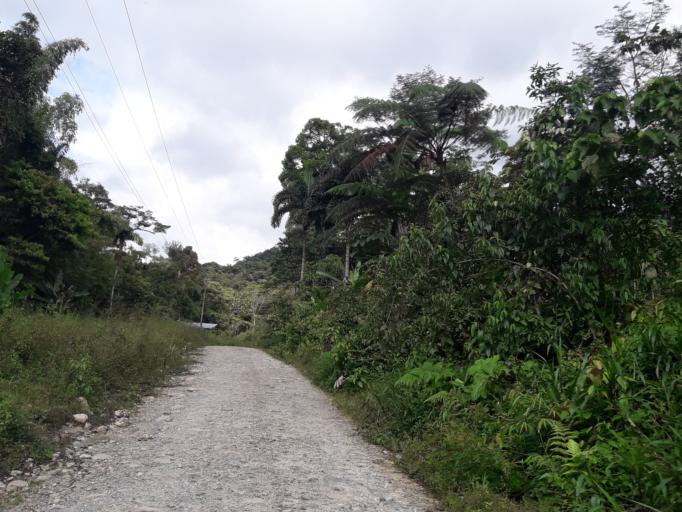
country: EC
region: Napo
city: Archidona
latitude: -0.9450
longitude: -77.8889
